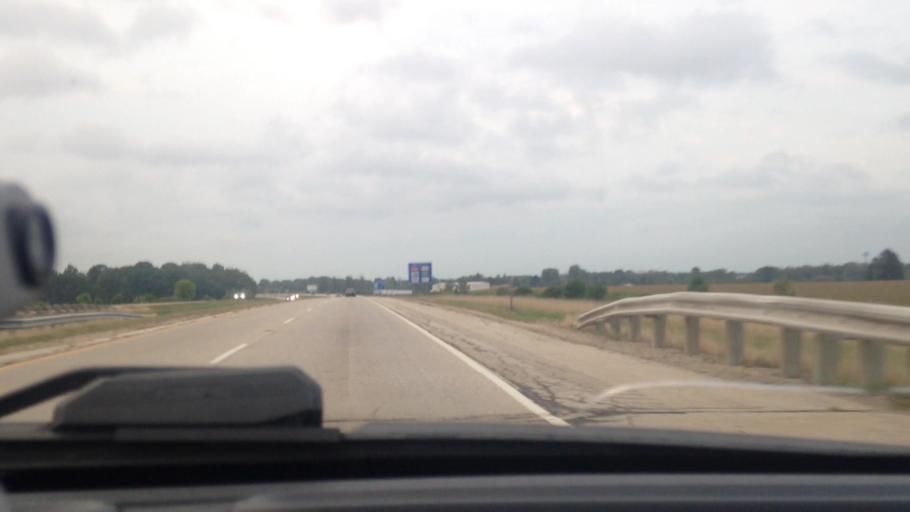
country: US
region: Wisconsin
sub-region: Washington County
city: Jackson
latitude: 43.3098
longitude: -88.1848
